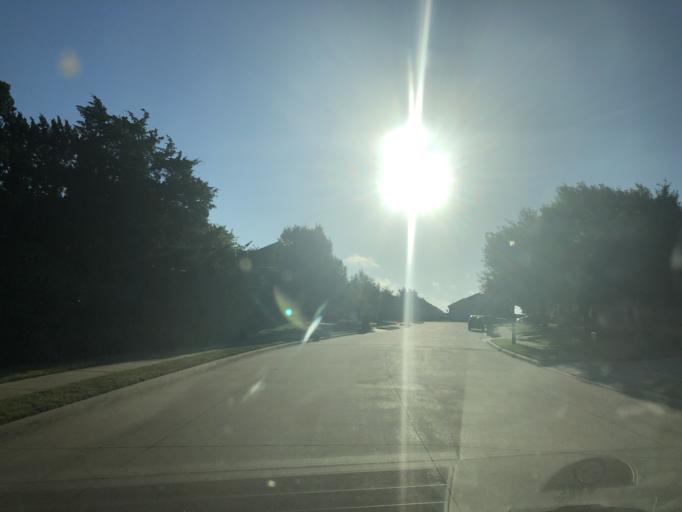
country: US
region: Texas
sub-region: Dallas County
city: Duncanville
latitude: 32.6514
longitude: -96.9501
